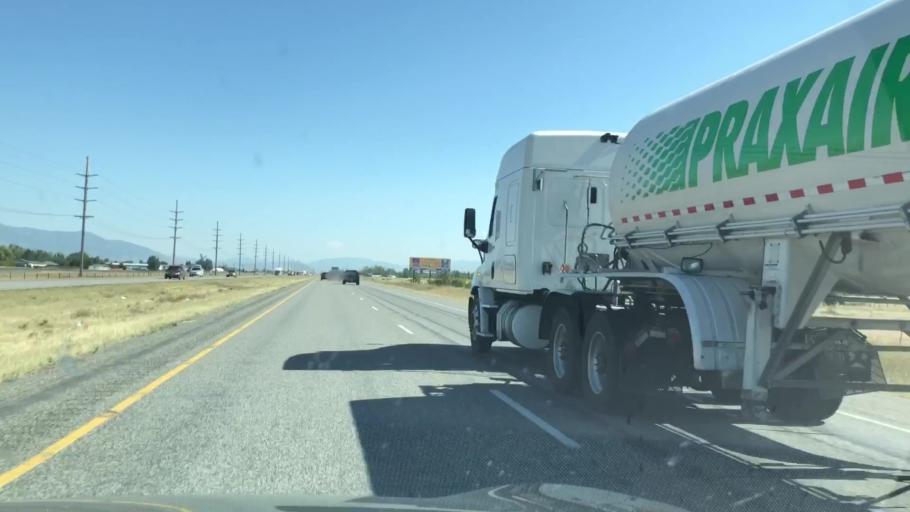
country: US
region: Montana
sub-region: Gallatin County
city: Belgrade
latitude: 45.8061
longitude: -111.2406
